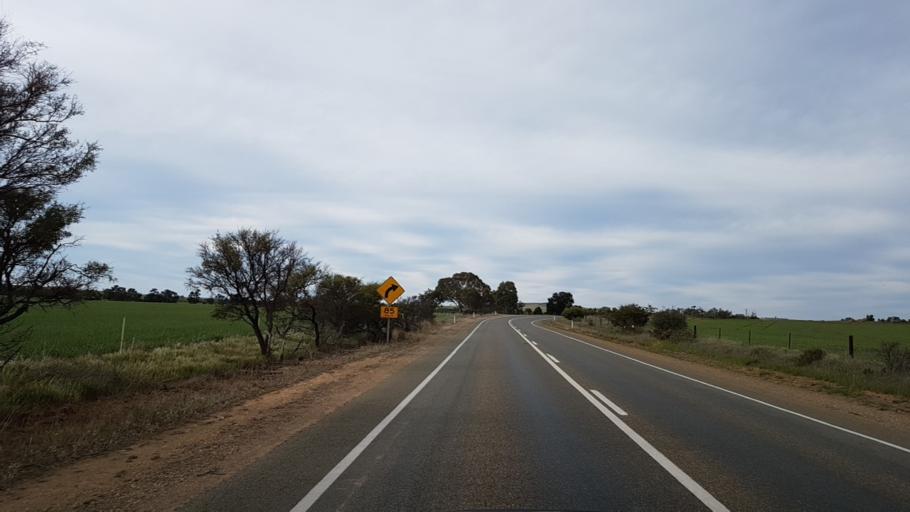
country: AU
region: South Australia
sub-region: Northern Areas
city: Jamestown
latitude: -33.2291
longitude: 138.3944
